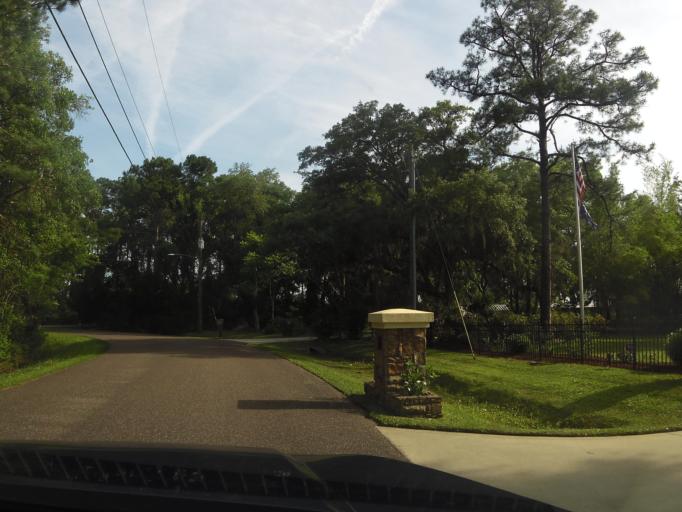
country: US
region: Florida
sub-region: Nassau County
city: Fernandina Beach
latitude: 30.5129
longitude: -81.4851
